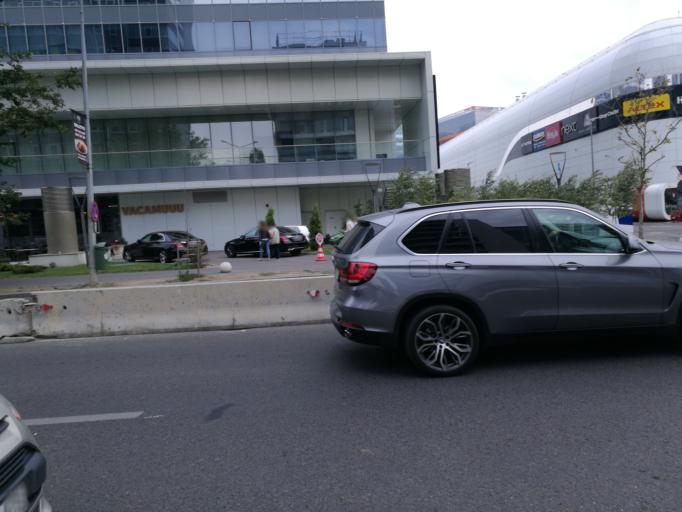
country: RO
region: Bucuresti
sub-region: Municipiul Bucuresti
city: Bucharest
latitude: 44.4789
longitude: 26.1016
